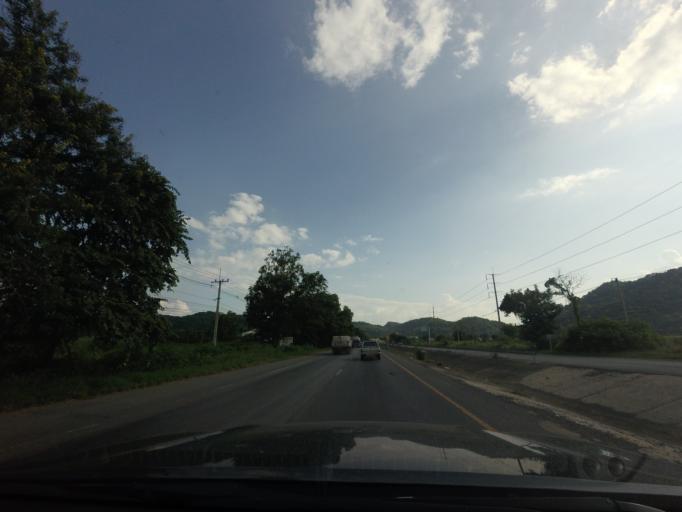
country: TH
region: Lop Buri
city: Phatthana Nikhom
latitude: 14.7717
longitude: 100.9134
